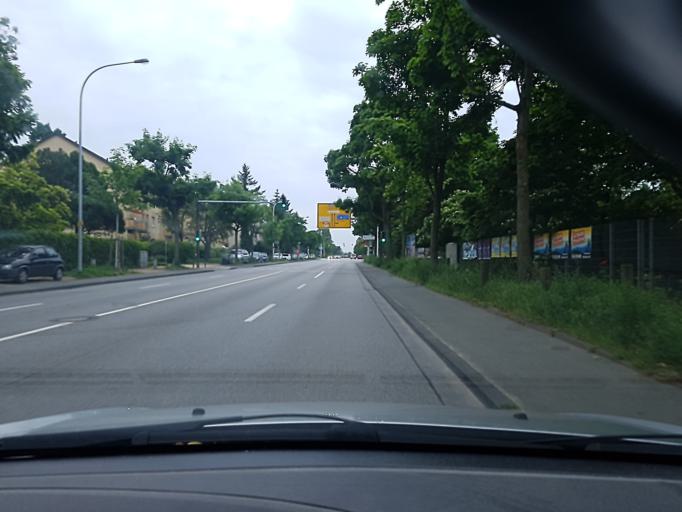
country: DE
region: Hesse
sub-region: Regierungsbezirk Darmstadt
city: Darmstadt
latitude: 49.8555
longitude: 8.6438
